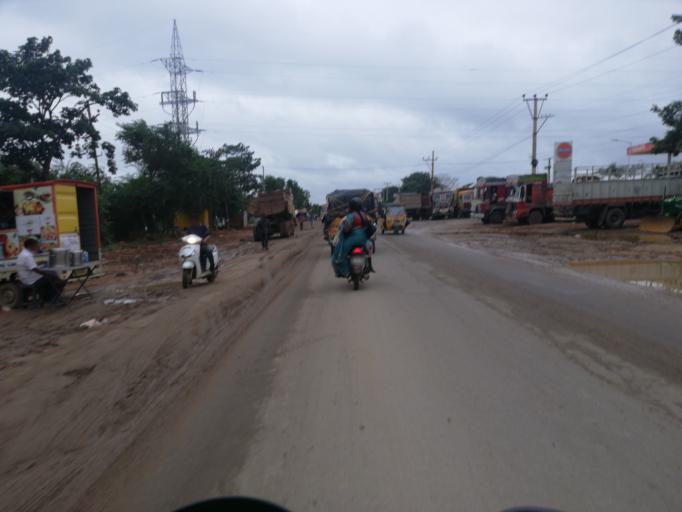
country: IN
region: Telangana
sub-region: Rangareddi
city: Quthbullapur
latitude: 17.5730
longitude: 78.4212
